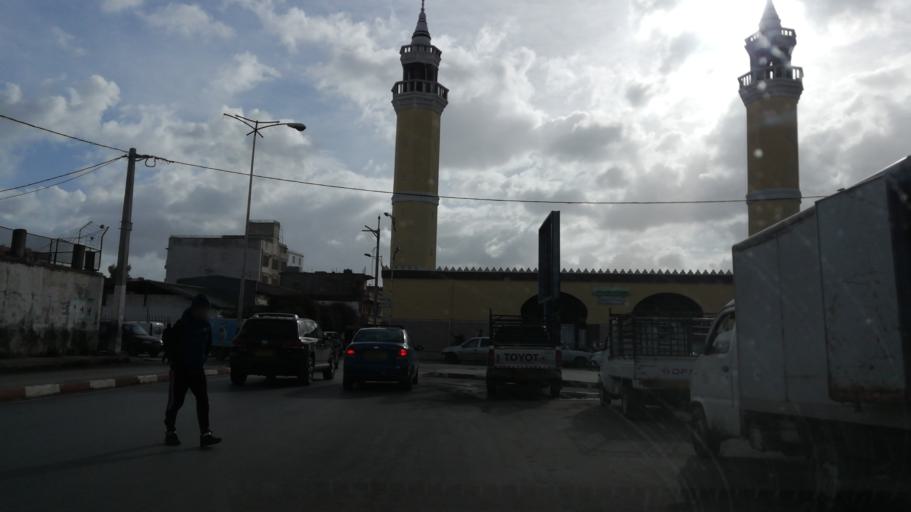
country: DZ
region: Oran
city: Oran
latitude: 35.6840
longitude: -0.6155
